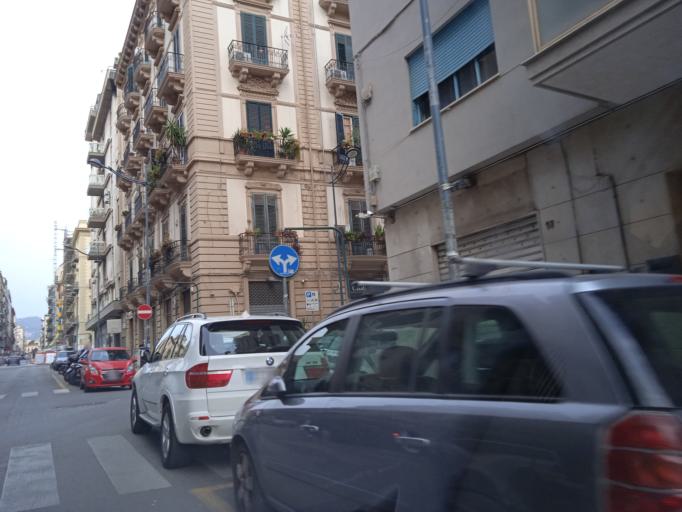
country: IT
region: Sicily
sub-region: Palermo
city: Palermo
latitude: 38.1241
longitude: 13.3606
